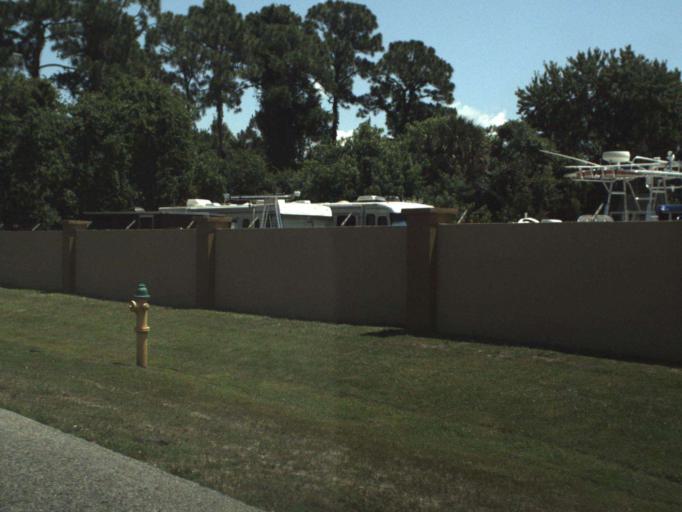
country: US
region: Florida
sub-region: Brevard County
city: Sharpes
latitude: 28.4413
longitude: -80.7088
